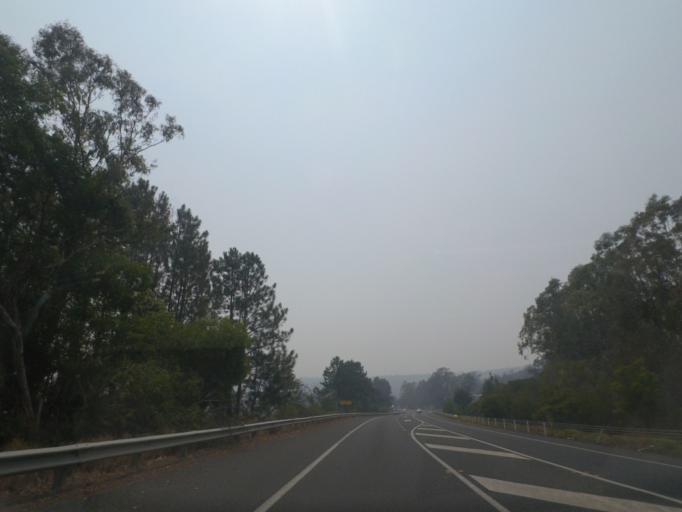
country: AU
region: New South Wales
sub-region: Clarence Valley
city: Maclean
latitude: -29.5647
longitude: 153.1414
